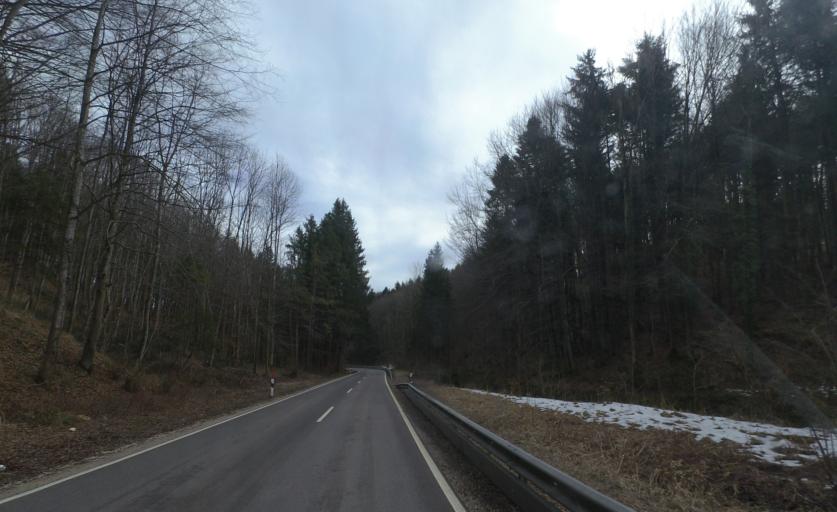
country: DE
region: Bavaria
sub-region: Upper Bavaria
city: Teisendorf
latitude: 47.8333
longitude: 12.7669
